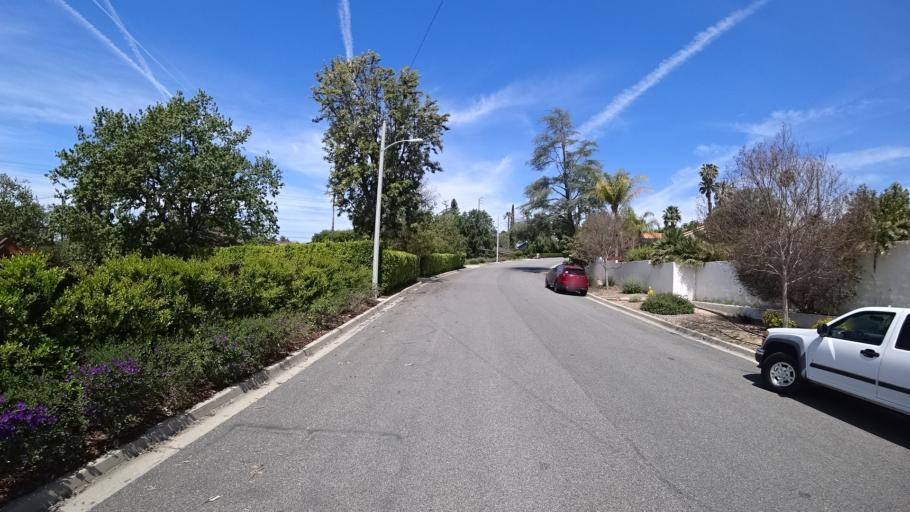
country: US
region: California
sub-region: Ventura County
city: Thousand Oaks
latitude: 34.2040
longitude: -118.8500
